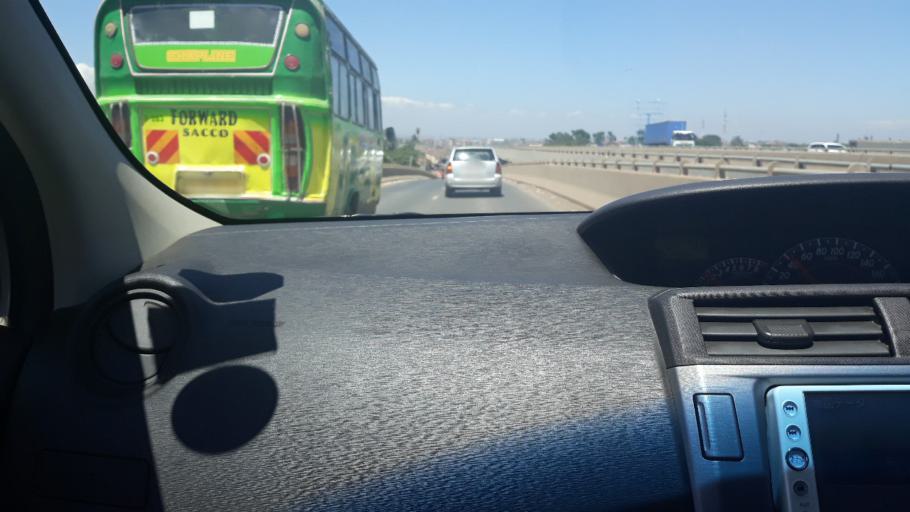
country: KE
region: Nairobi Area
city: Pumwani
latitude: -1.2741
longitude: 36.8815
